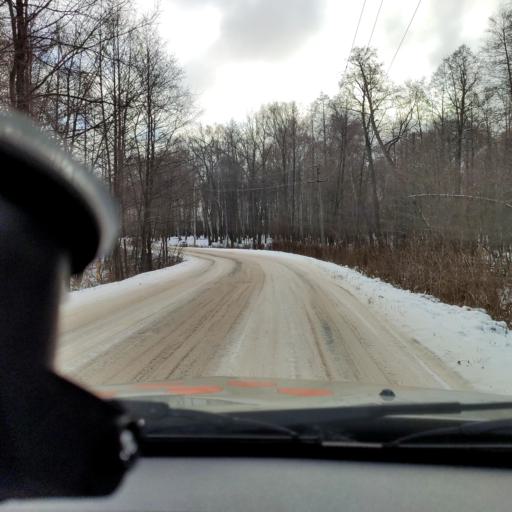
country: RU
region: Bashkortostan
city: Avdon
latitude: 54.7813
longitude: 55.7500
